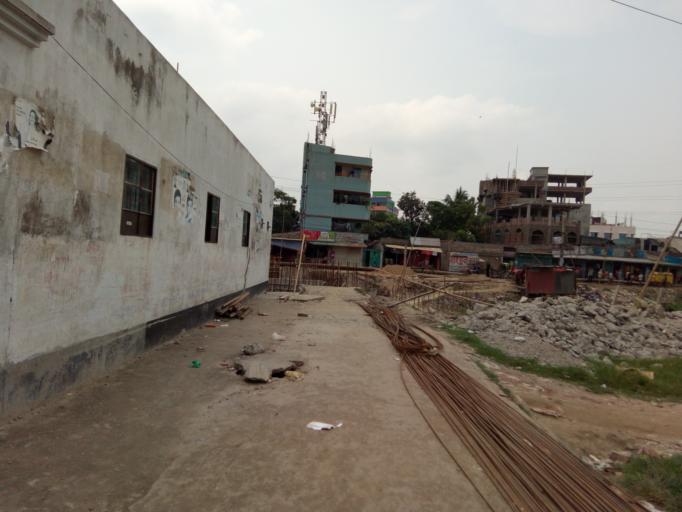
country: BD
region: Dhaka
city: Paltan
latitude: 23.7504
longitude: 90.4494
